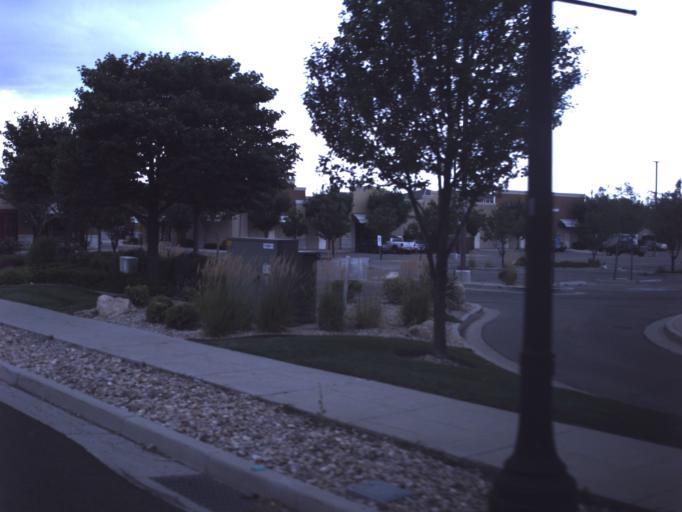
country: US
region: Utah
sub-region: Salt Lake County
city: Draper
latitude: 40.5269
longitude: -111.8836
